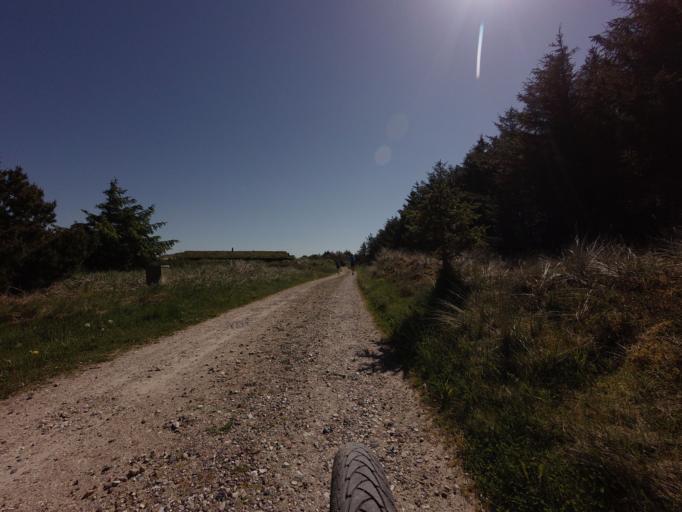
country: DK
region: North Denmark
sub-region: Jammerbugt Kommune
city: Pandrup
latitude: 57.3046
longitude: 9.6524
